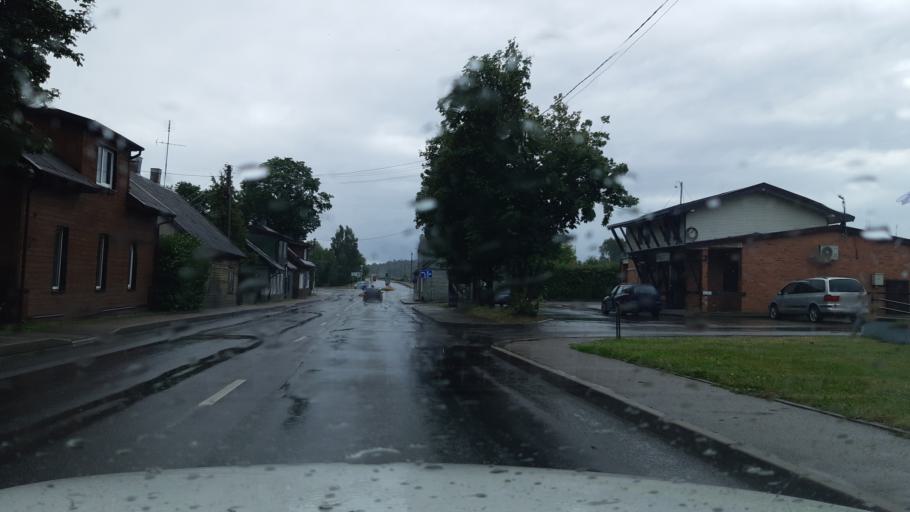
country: LT
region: Taurages apskritis
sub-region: Jurbarkas
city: Jurbarkas
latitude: 55.0781
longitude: 22.7611
